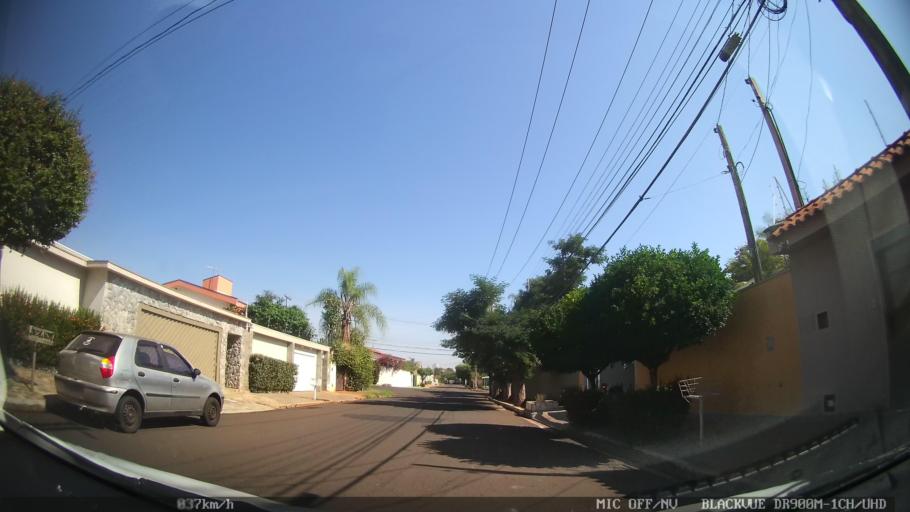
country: BR
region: Sao Paulo
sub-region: Ribeirao Preto
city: Ribeirao Preto
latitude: -21.1990
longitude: -47.7816
